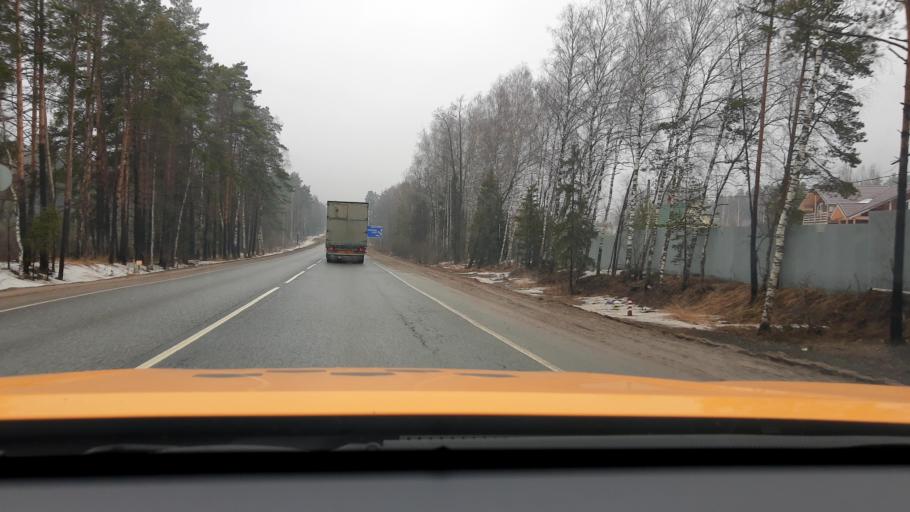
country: RU
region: Moskovskaya
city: Chernogolovka
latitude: 55.9957
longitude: 38.3207
